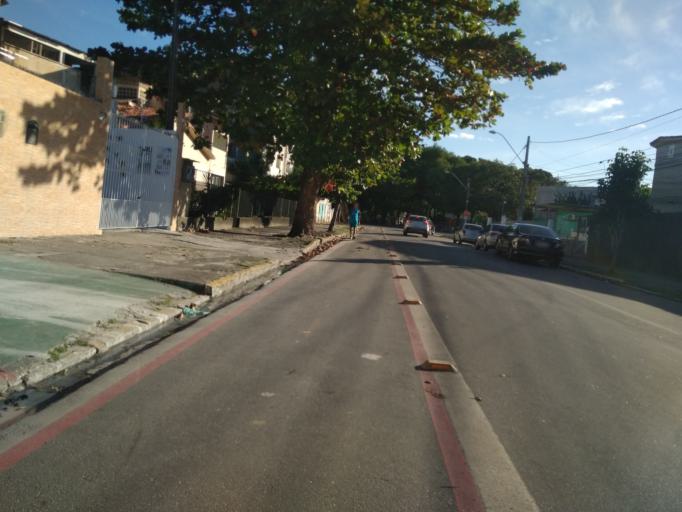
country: BR
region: Pernambuco
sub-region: Recife
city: Recife
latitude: -8.0811
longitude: -34.9373
